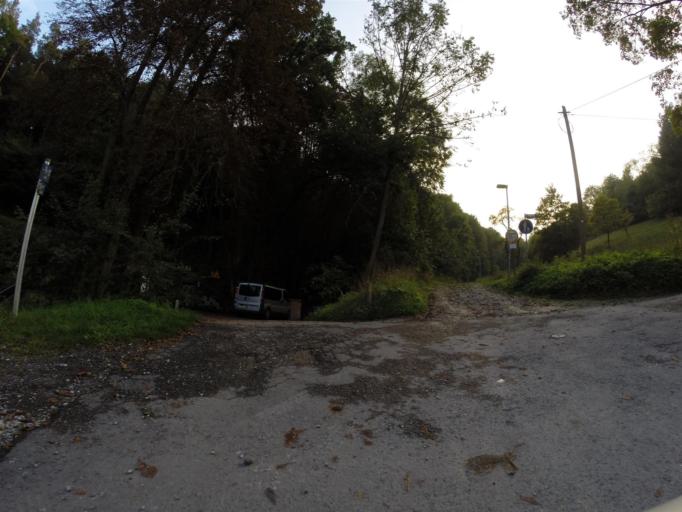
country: DE
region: Thuringia
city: Jena
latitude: 50.9200
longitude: 11.5583
